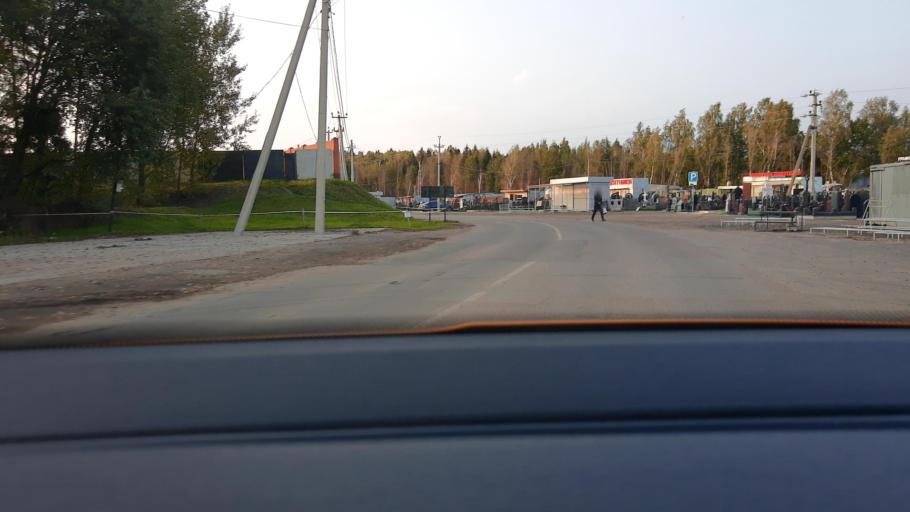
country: RU
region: Moskovskaya
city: Lobnya
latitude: 55.9999
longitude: 37.4006
